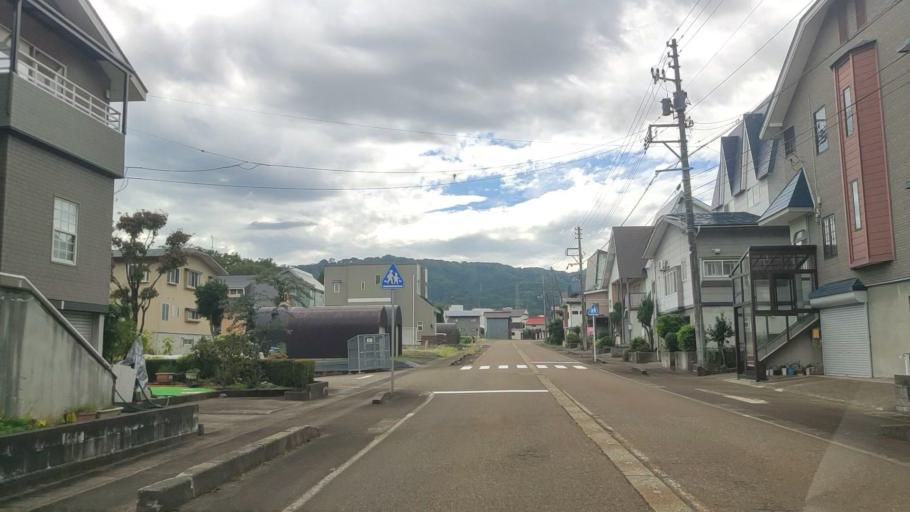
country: JP
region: Niigata
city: Arai
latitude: 37.0088
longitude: 138.2581
